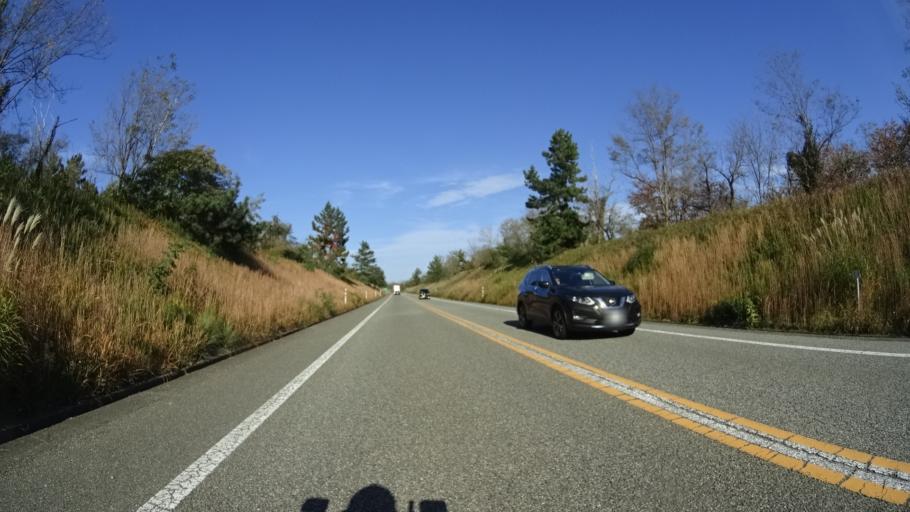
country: JP
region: Ishikawa
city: Kanazawa-shi
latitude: 36.6422
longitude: 136.6336
